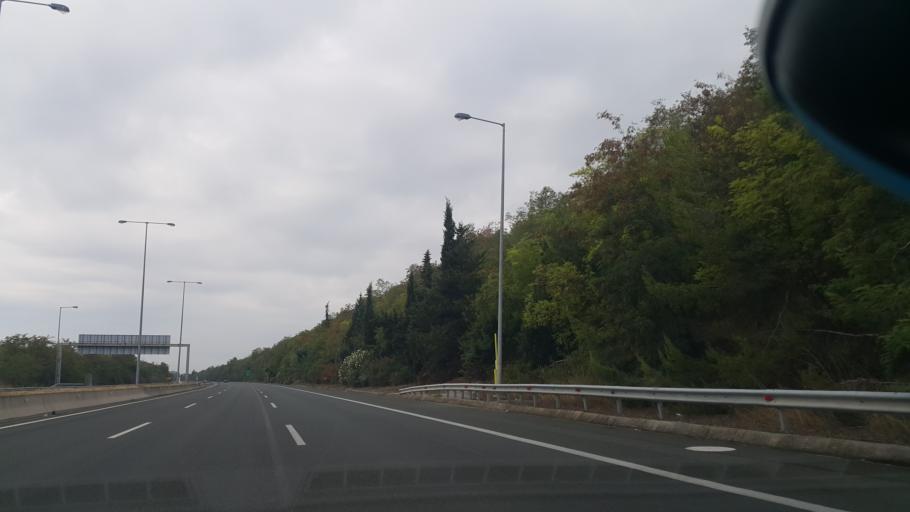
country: GR
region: Central Macedonia
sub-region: Nomos Pierias
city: Makrygialos
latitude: 40.4106
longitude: 22.5931
